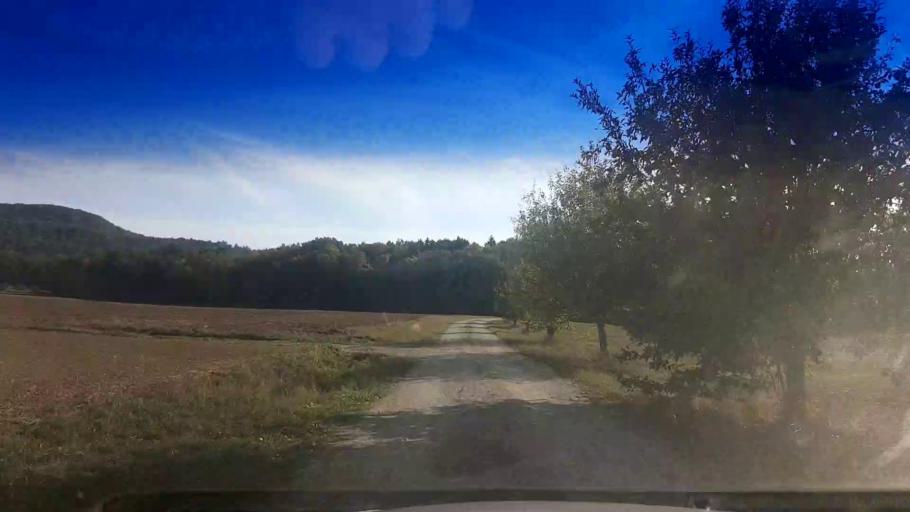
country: DE
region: Bavaria
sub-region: Upper Franconia
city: Schesslitz
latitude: 49.9508
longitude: 11.0259
